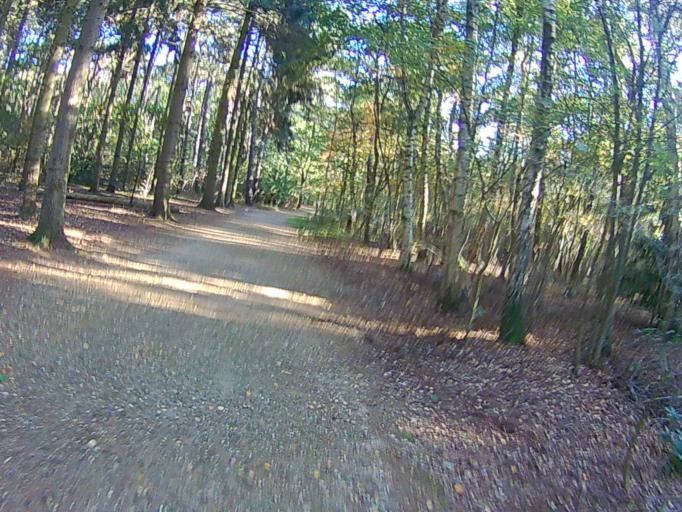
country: BE
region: Flanders
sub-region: Provincie Antwerpen
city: Stabroek
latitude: 51.3388
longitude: 4.3915
